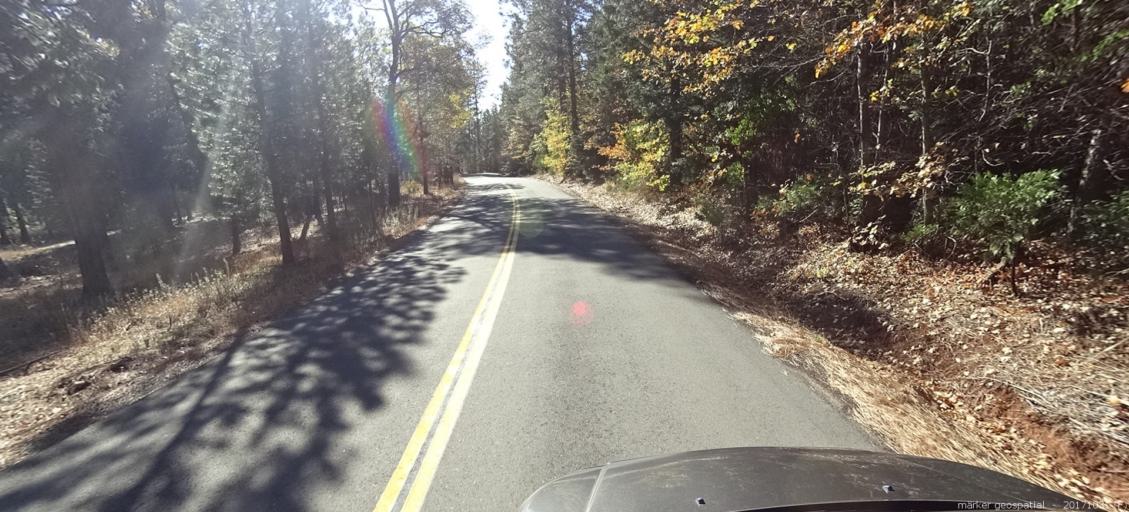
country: US
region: California
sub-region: Shasta County
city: Shingletown
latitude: 40.4821
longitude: -121.8766
